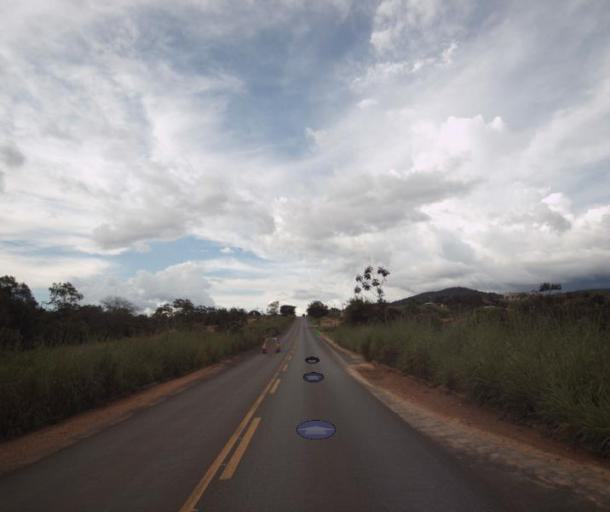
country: BR
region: Goias
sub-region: Niquelandia
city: Niquelandia
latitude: -14.4793
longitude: -48.4889
